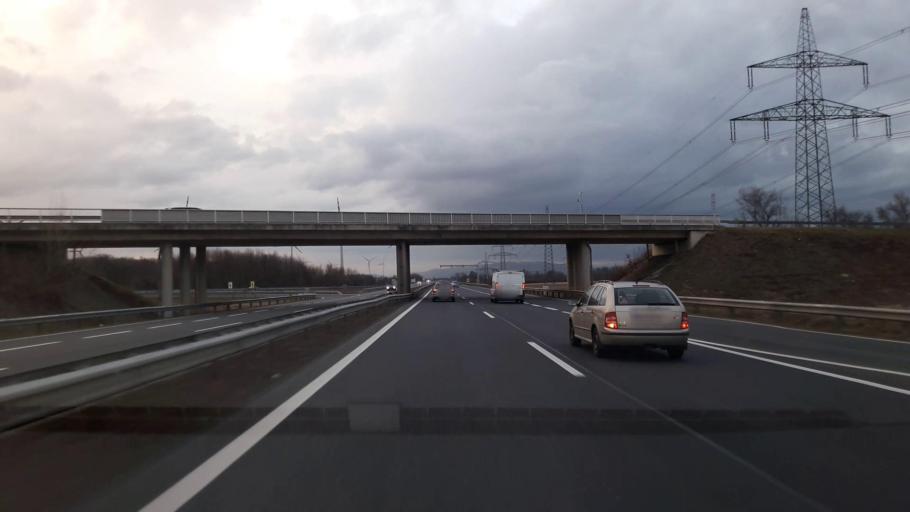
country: AT
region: Lower Austria
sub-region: Politischer Bezirk Baden
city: Ebreichsdorf
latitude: 47.9280
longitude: 16.3922
